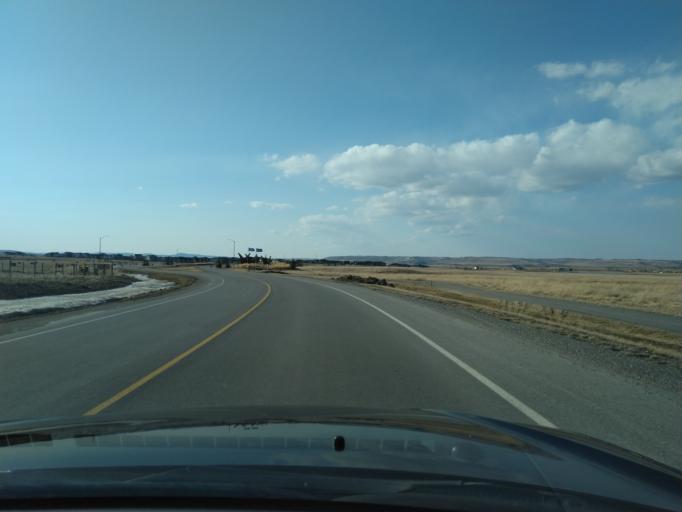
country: CA
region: Alberta
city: Cochrane
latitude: 51.1029
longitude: -114.3884
